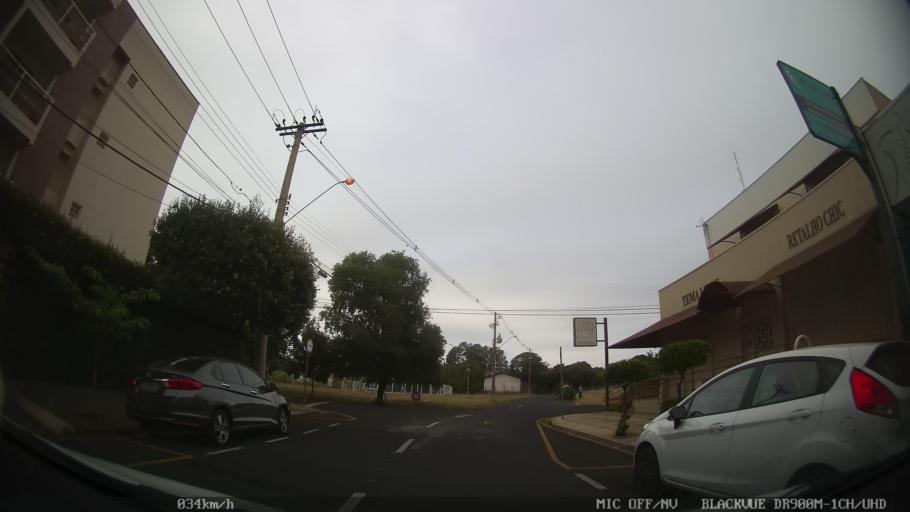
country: BR
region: Sao Paulo
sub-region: Sao Jose Do Rio Preto
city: Sao Jose do Rio Preto
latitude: -20.8396
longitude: -49.3842
